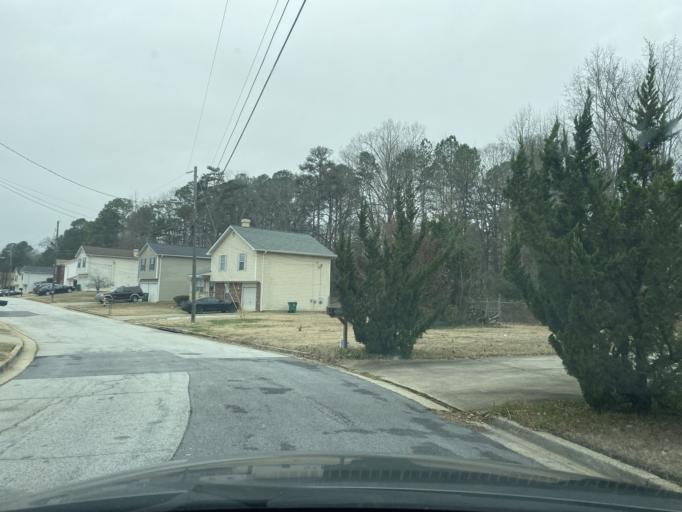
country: US
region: Georgia
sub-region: DeKalb County
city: Pine Mountain
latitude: 33.6943
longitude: -84.1594
